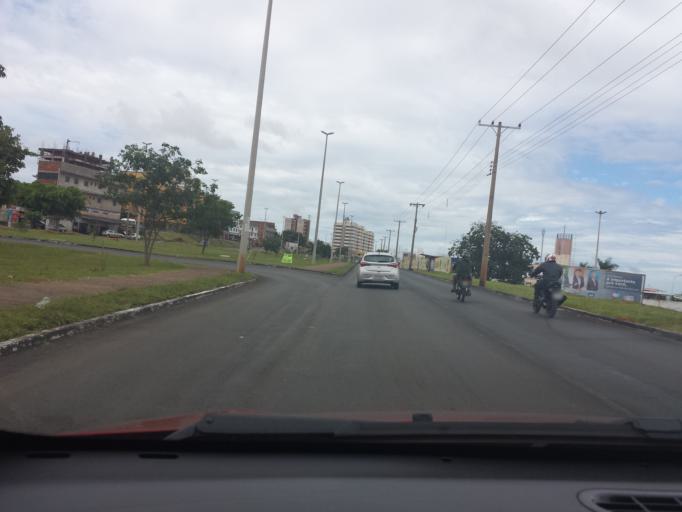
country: BR
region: Federal District
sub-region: Brasilia
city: Brasilia
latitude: -15.8606
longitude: -48.0859
